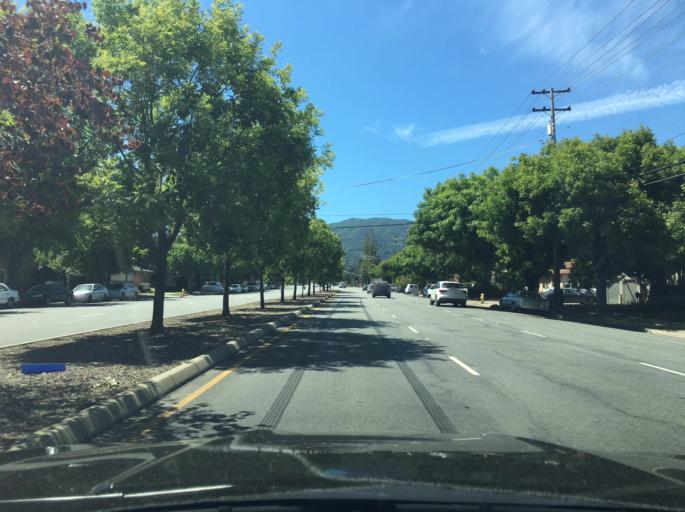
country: US
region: California
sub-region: Santa Clara County
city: Cambrian Park
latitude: 37.2384
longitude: -121.9036
